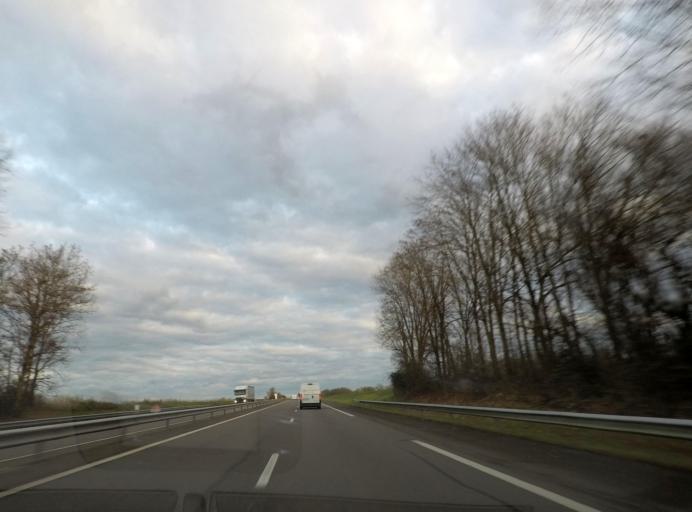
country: FR
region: Rhone-Alpes
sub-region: Departement de l'Ain
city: Saint-Cyr-sur-Menthon
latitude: 46.2825
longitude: 4.9580
